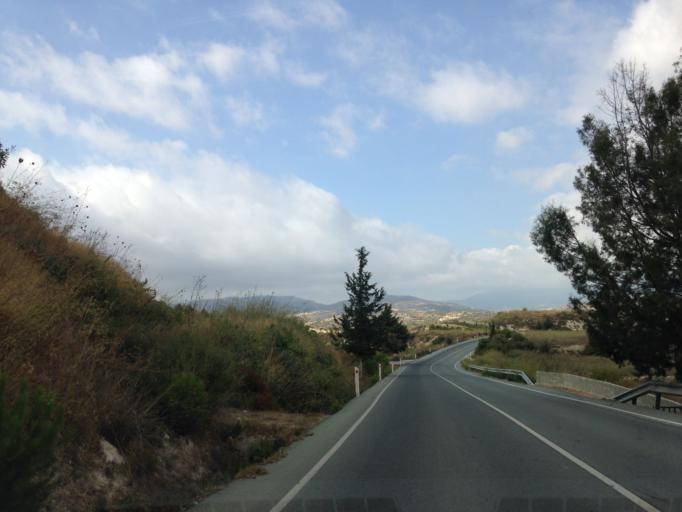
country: CY
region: Limassol
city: Pachna
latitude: 34.7866
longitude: 32.7971
